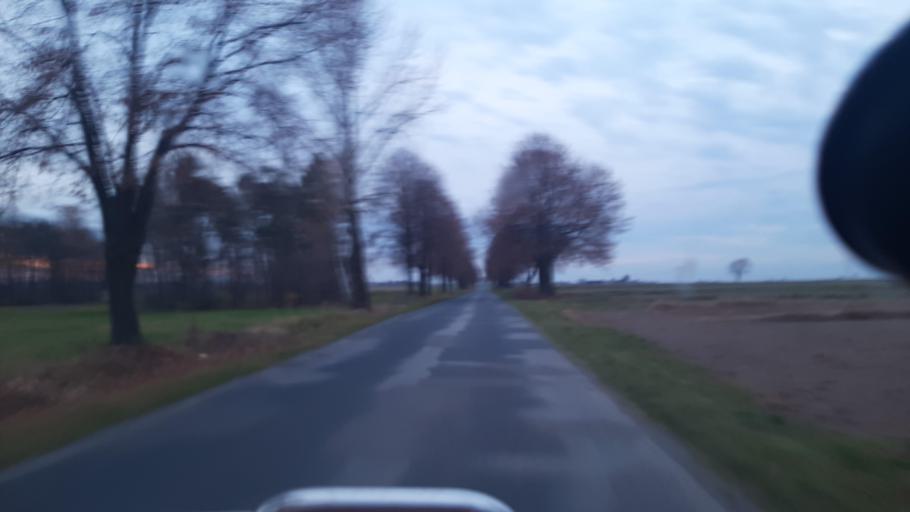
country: PL
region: Lublin Voivodeship
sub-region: Powiat lubelski
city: Garbow
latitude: 51.3788
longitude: 22.3748
